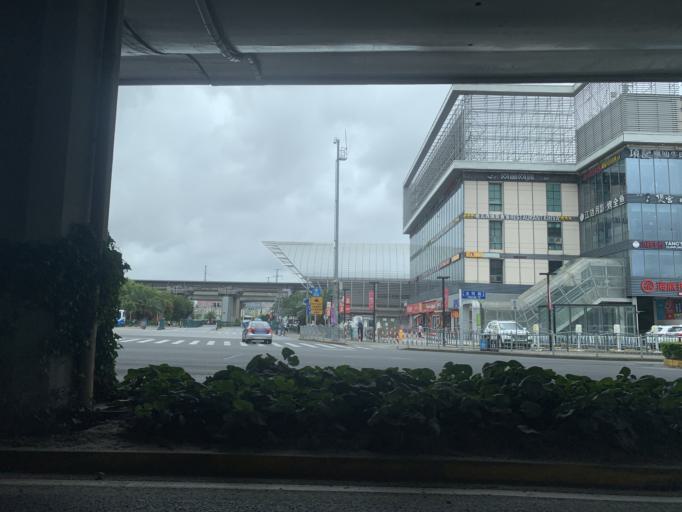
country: CN
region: Shanghai Shi
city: Huamu
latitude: 31.2057
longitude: 121.5548
